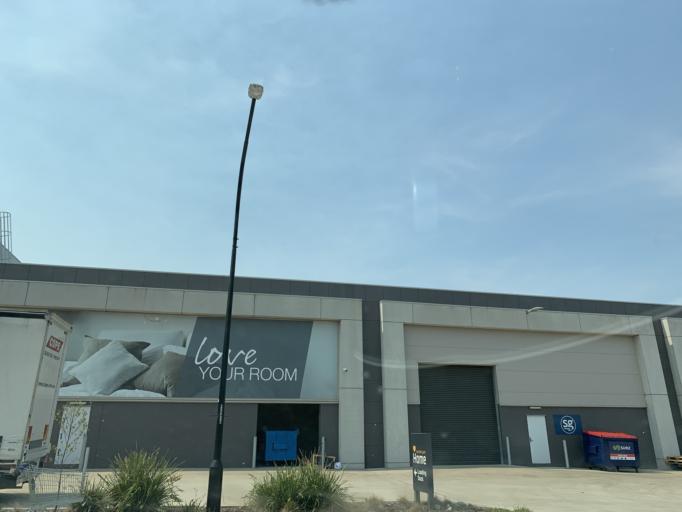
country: AU
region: New South Wales
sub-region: Blacktown
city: Hassall Grove
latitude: -33.7209
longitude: 150.8401
